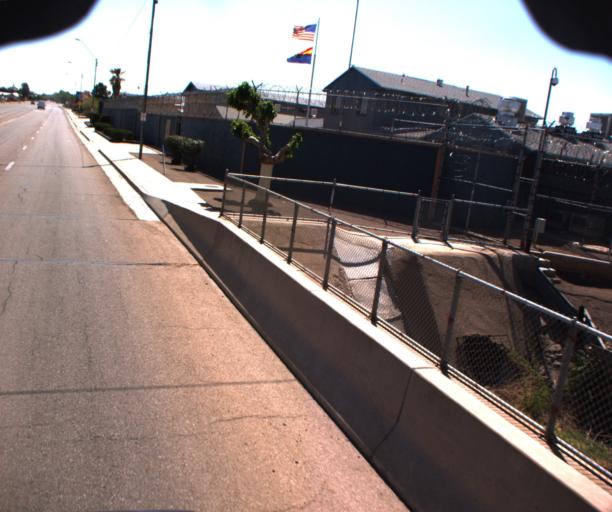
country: US
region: Arizona
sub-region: Cochise County
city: Pirtleville
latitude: 31.3506
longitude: -109.5624
